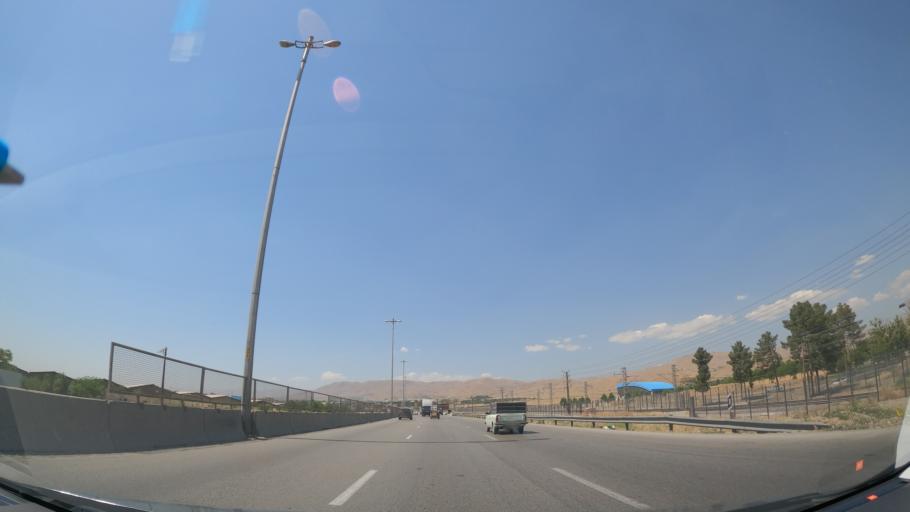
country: IR
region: Alborz
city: Karaj
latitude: 35.8540
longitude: 50.9087
